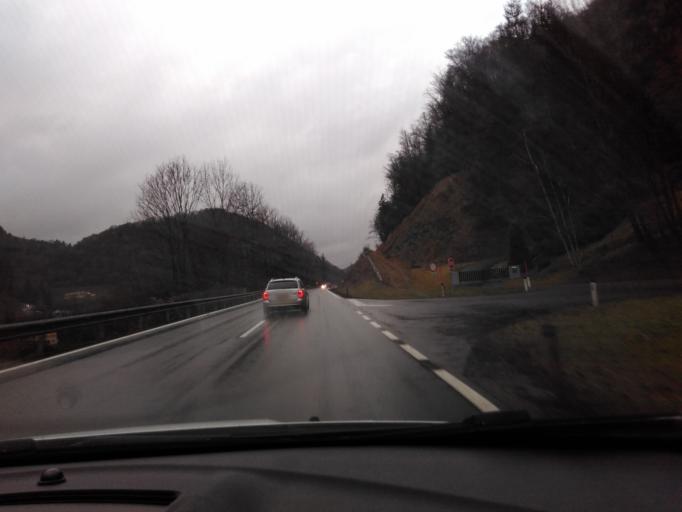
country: AT
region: Upper Austria
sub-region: Politischer Bezirk Urfahr-Umgebung
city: Kirchschlag bei Linz
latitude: 48.3781
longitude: 14.2925
